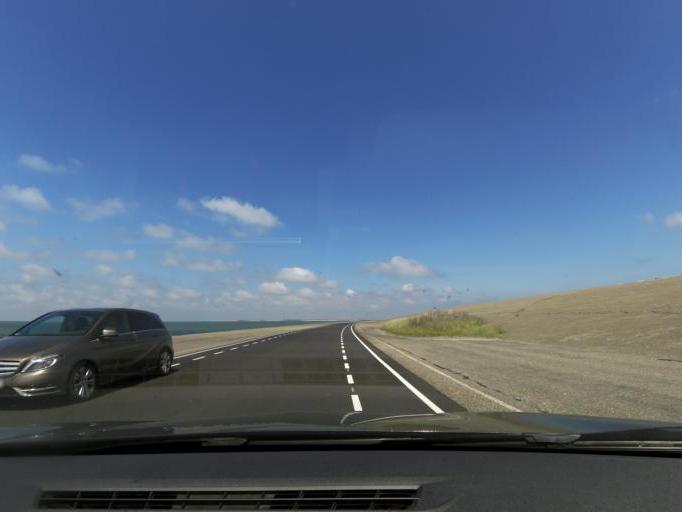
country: NL
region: Zeeland
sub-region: Schouwen-Duiveland
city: Scharendijke
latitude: 51.7531
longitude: 3.8283
